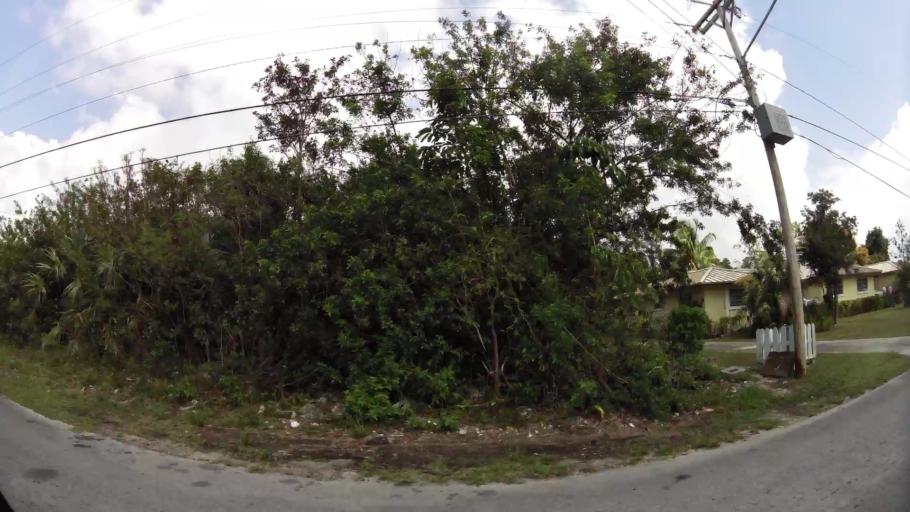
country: BS
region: Freeport
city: Lucaya
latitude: 26.5194
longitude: -78.6553
